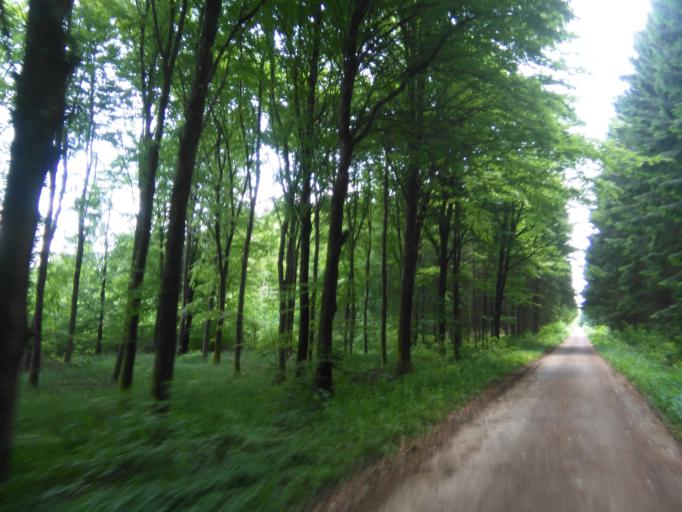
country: DK
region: Central Jutland
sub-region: Favrskov Kommune
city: Hinnerup
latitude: 56.2621
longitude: 10.0491
